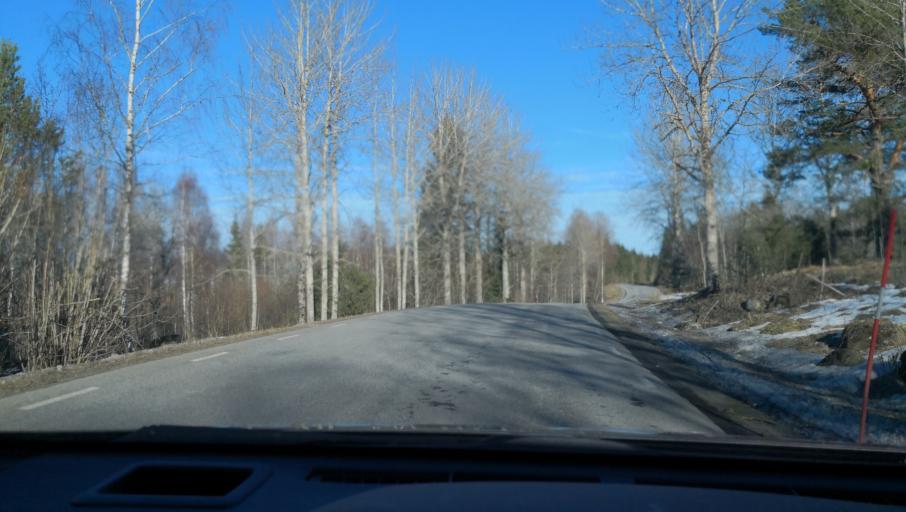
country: SE
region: Uppsala
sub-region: Osthammars Kommun
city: Osterbybruk
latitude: 60.2401
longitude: 17.9255
